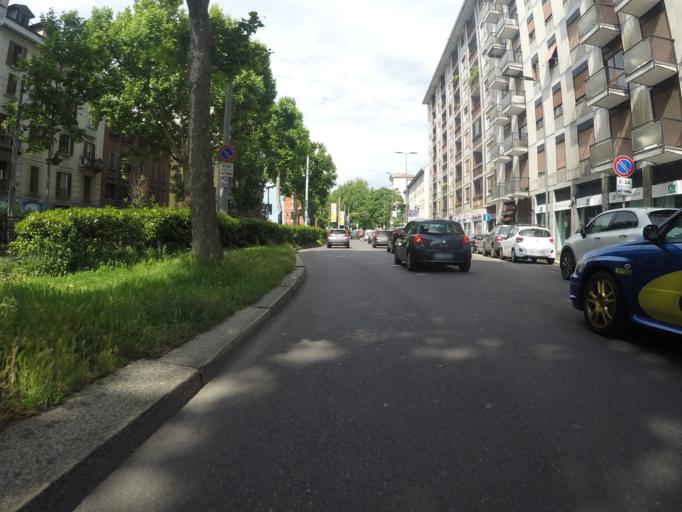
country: IT
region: Lombardy
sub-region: Citta metropolitana di Milano
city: Milano
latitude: 45.4437
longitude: 9.1780
